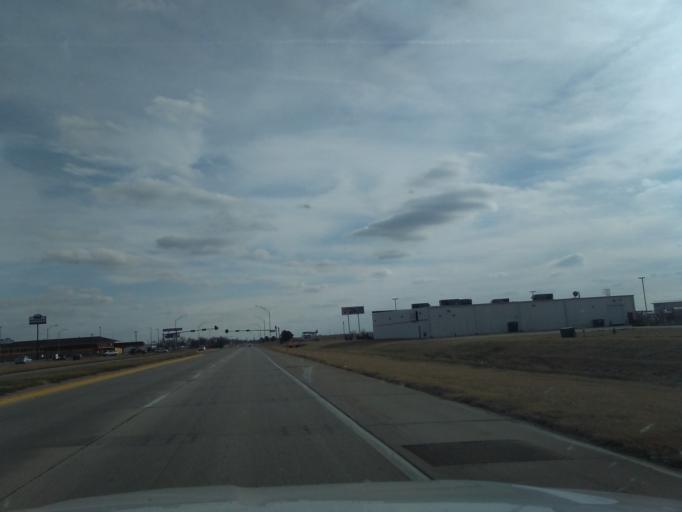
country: US
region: Nebraska
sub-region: Gage County
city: Beatrice
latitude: 40.3040
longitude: -96.7470
